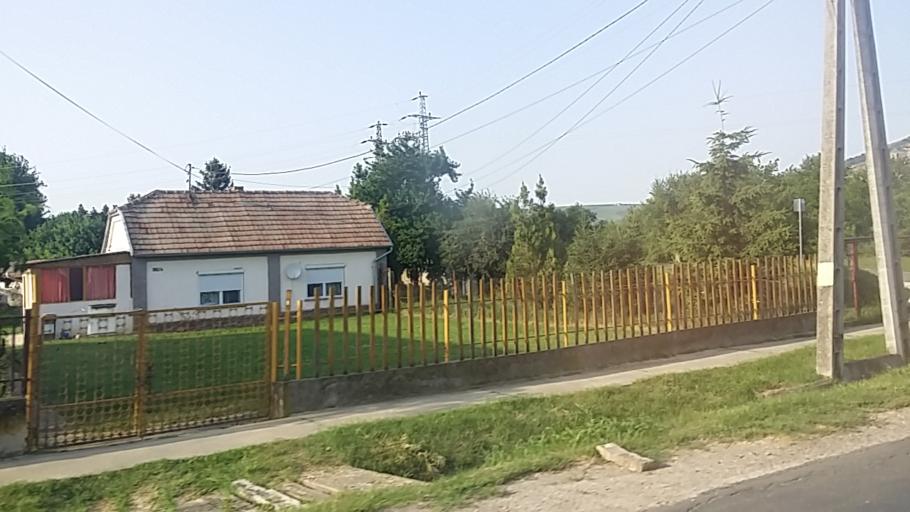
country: HU
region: Baranya
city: Villany
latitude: 45.8482
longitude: 18.3828
